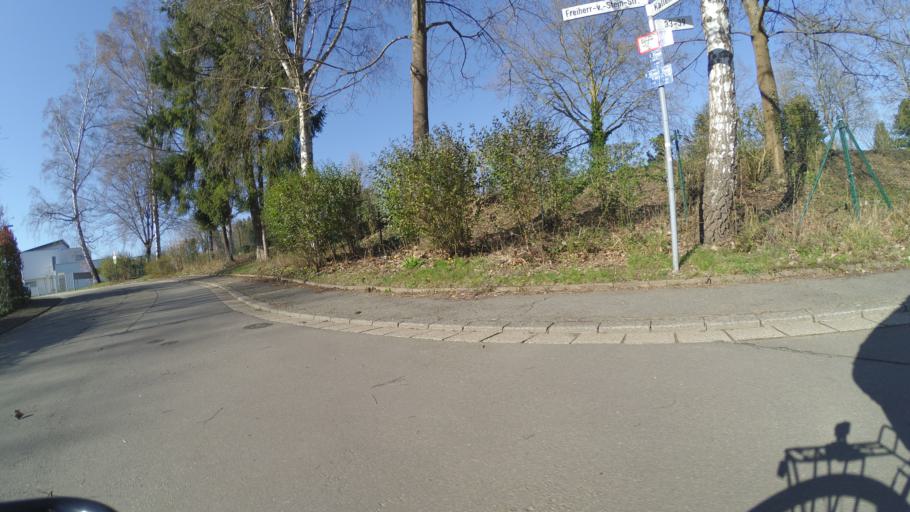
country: DE
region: Saarland
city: Neunkirchen
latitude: 49.3721
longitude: 7.1713
